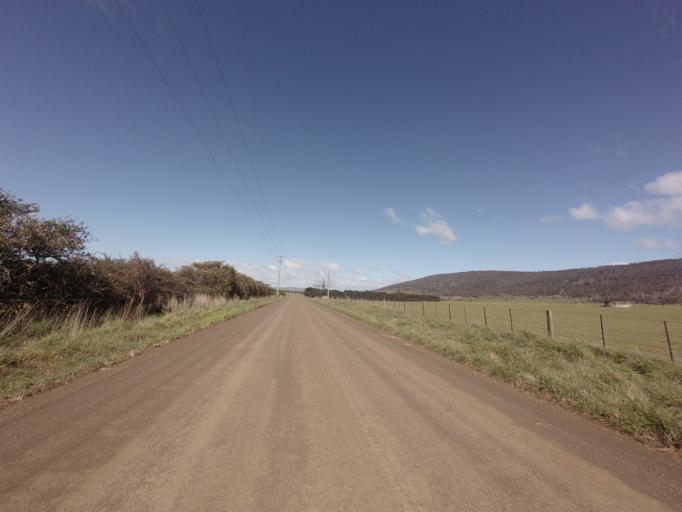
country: AU
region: Tasmania
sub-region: Northern Midlands
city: Evandale
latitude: -41.9510
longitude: 147.4350
